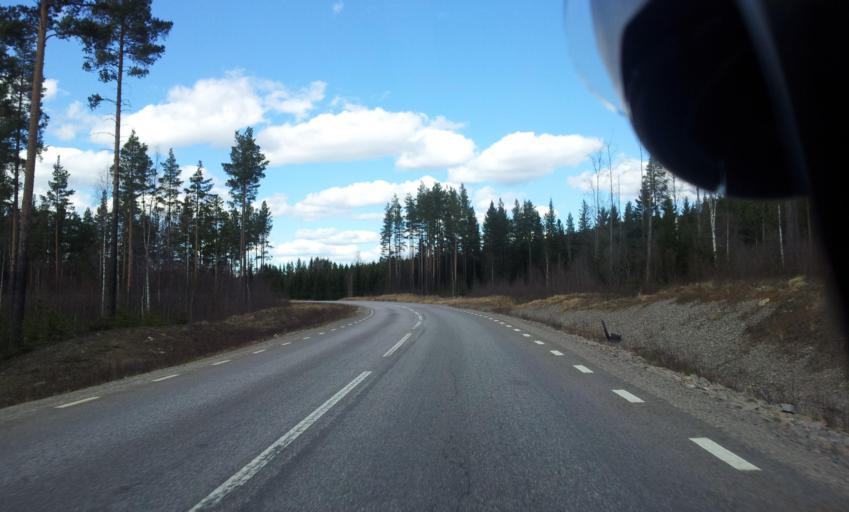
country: SE
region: Gaevleborg
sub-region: Ovanakers Kommun
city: Edsbyn
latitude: 61.1725
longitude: 15.8842
